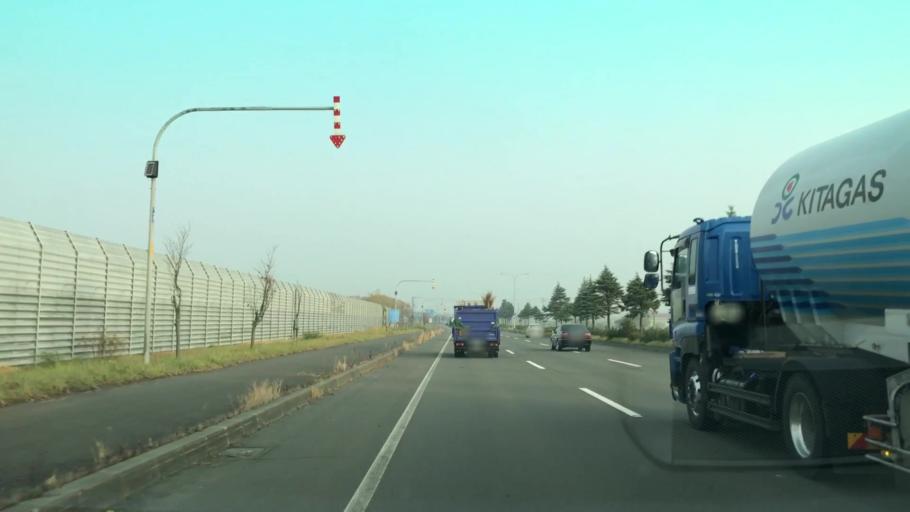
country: JP
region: Hokkaido
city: Ishikari
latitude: 43.1722
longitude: 141.3484
